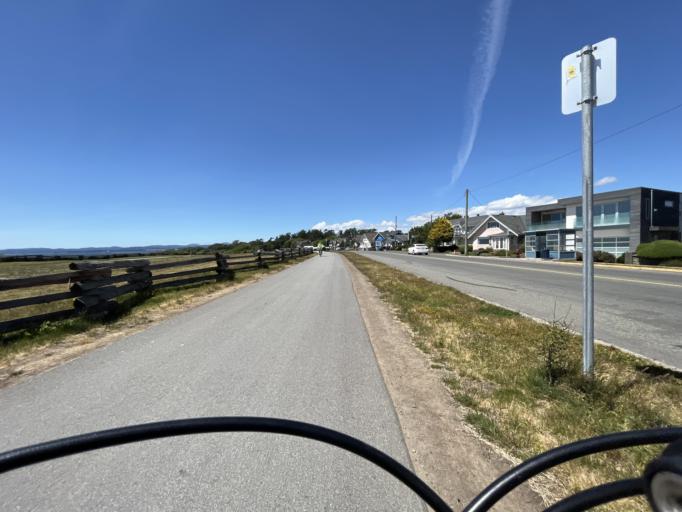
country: CA
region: British Columbia
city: Victoria
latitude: 48.4069
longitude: -123.3535
